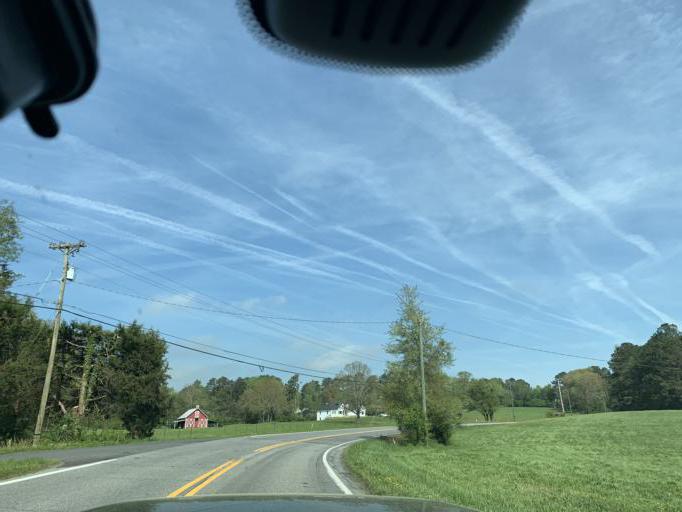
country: US
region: Georgia
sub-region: Forsyth County
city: Cumming
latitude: 34.2180
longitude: -84.0829
